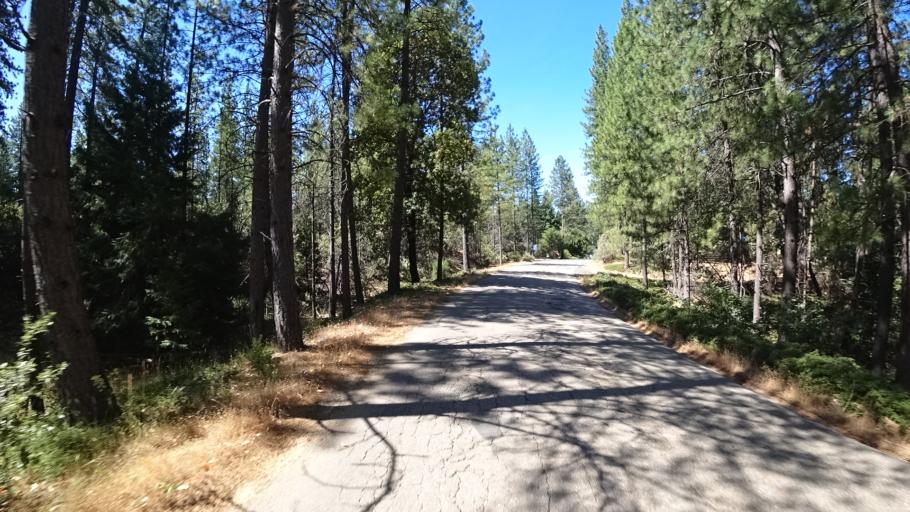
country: US
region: California
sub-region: Amador County
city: Pioneer
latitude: 38.4100
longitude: -120.5030
